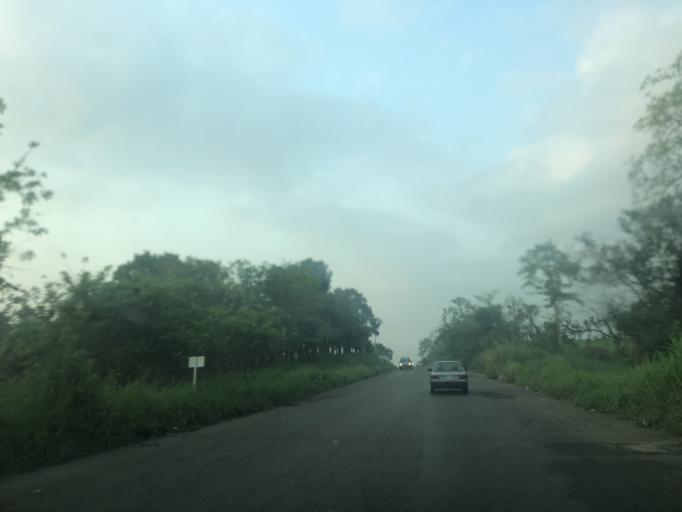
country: MX
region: Chiapas
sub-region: Reforma
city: El Carmen (El Limon)
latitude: 17.8405
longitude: -93.1645
